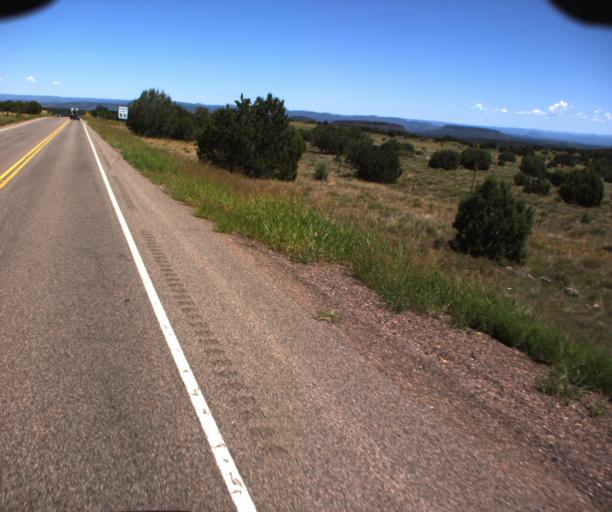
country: US
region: Arizona
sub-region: Navajo County
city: Cibecue
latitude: 33.7164
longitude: -110.5338
